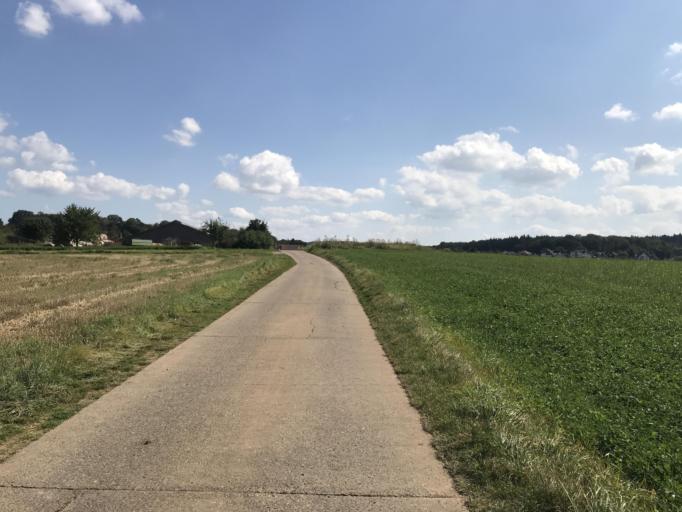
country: DE
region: Hesse
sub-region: Regierungsbezirk Giessen
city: Hungen
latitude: 50.4320
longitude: 8.9106
